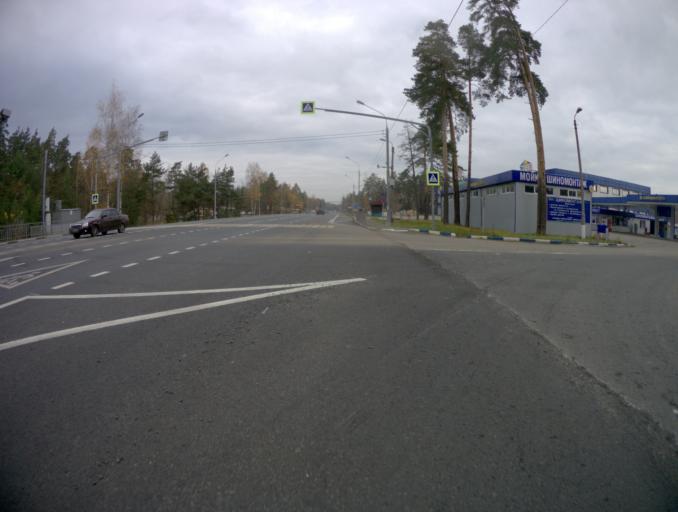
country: RU
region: Moskovskaya
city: Malaya Dubna
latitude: 55.8483
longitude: 38.9644
